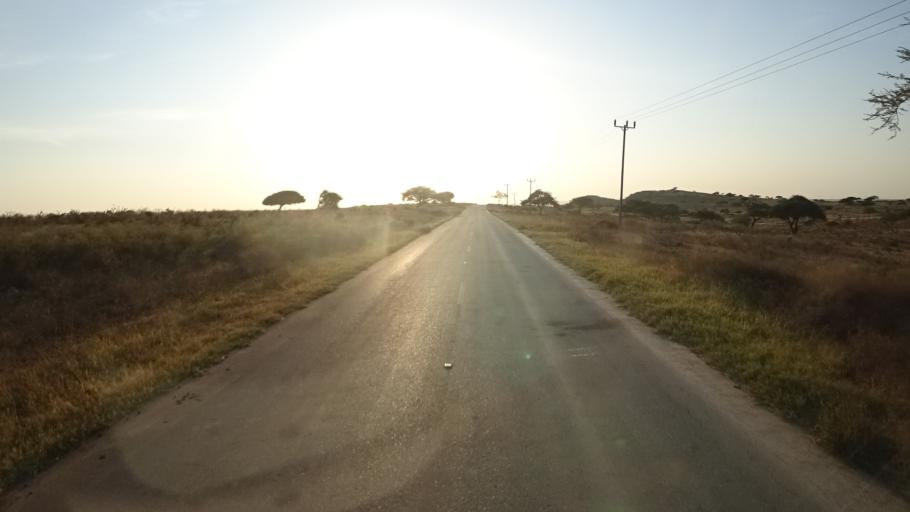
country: OM
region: Zufar
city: Salalah
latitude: 17.1476
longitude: 54.6114
